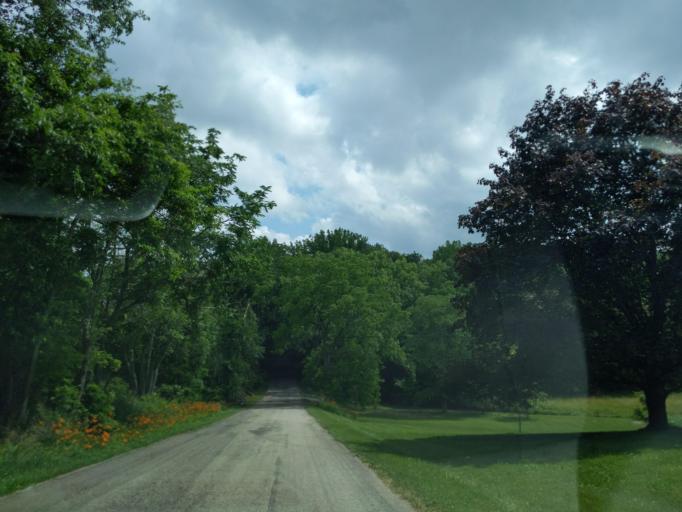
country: US
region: Indiana
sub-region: Ripley County
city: Batesville
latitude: 39.3292
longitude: -85.1899
